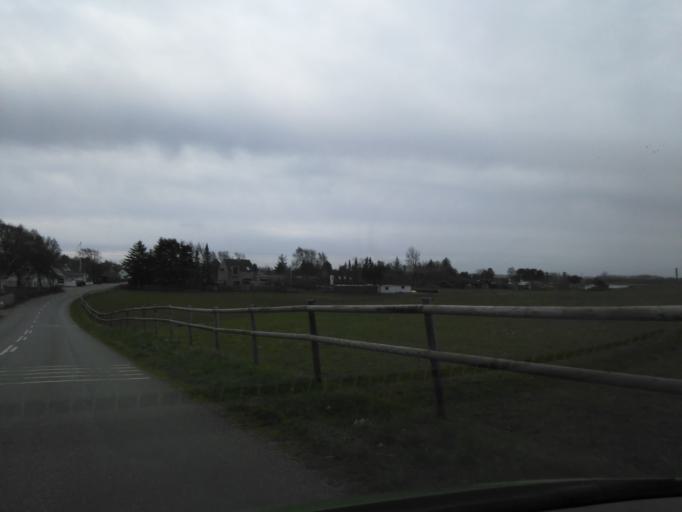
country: DK
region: Central Jutland
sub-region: Arhus Kommune
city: Beder
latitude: 56.0270
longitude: 10.2605
